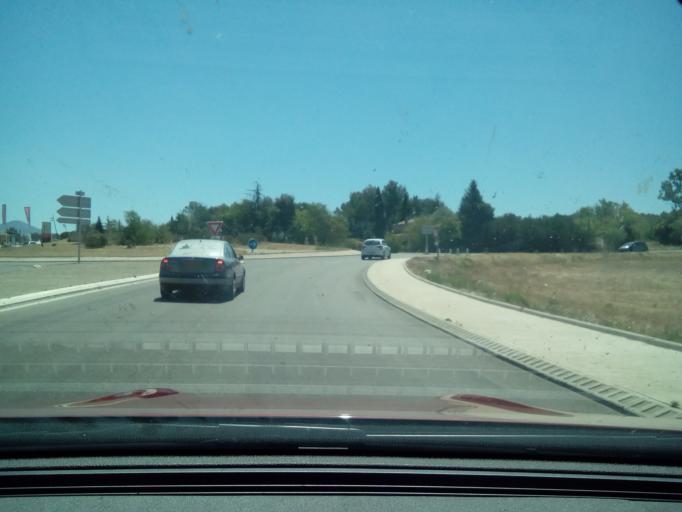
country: FR
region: Provence-Alpes-Cote d'Azur
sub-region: Departement des Bouches-du-Rhone
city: Rousset
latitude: 43.4639
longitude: 5.6103
